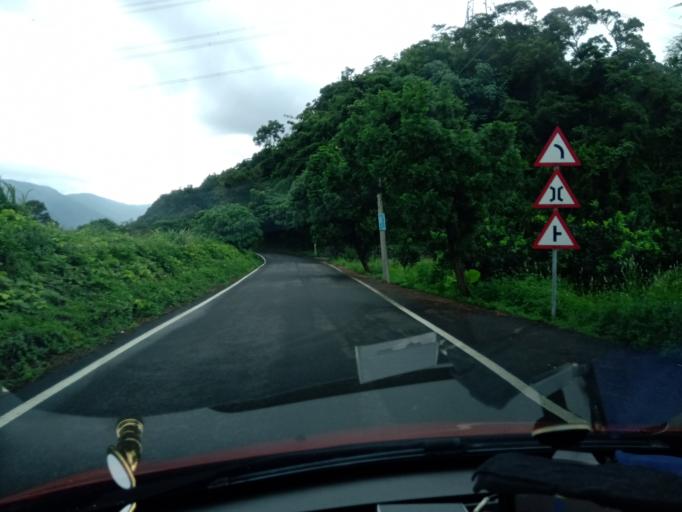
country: TW
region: Taiwan
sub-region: Yilan
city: Yilan
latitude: 24.7811
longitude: 121.7121
